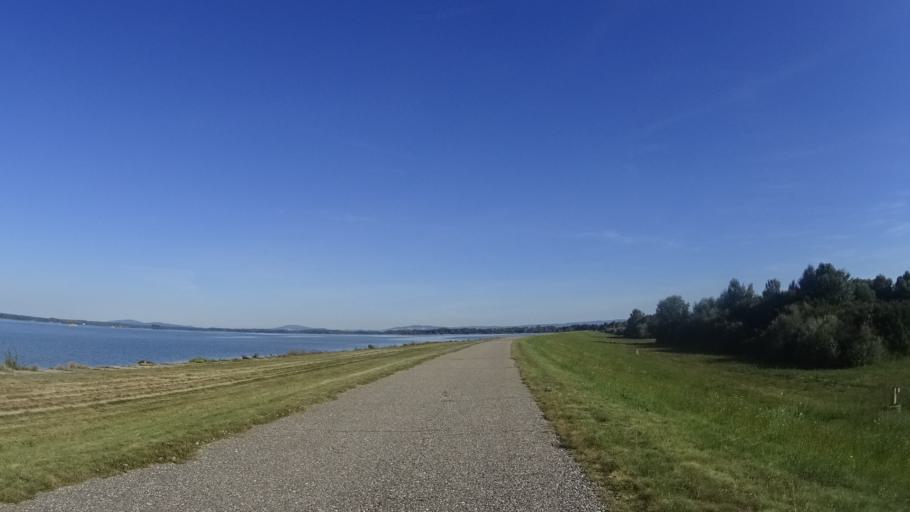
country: SK
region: Bratislavsky
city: Dunajska Luzna
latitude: 48.0359
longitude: 17.2439
